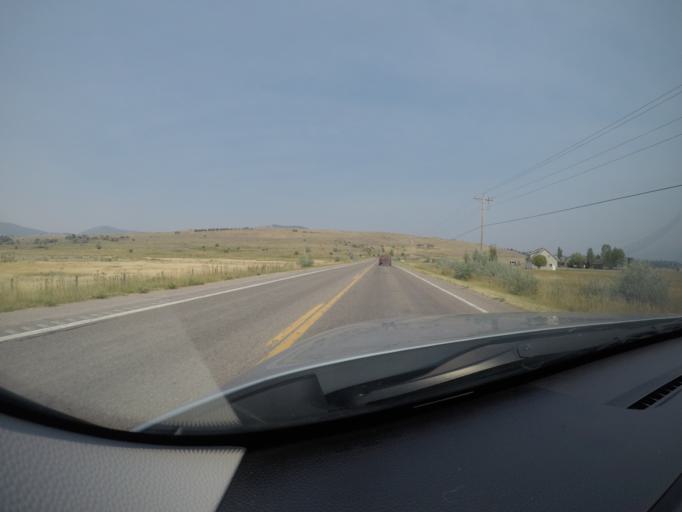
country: US
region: Montana
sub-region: Lake County
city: Polson
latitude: 47.7305
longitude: -114.1886
